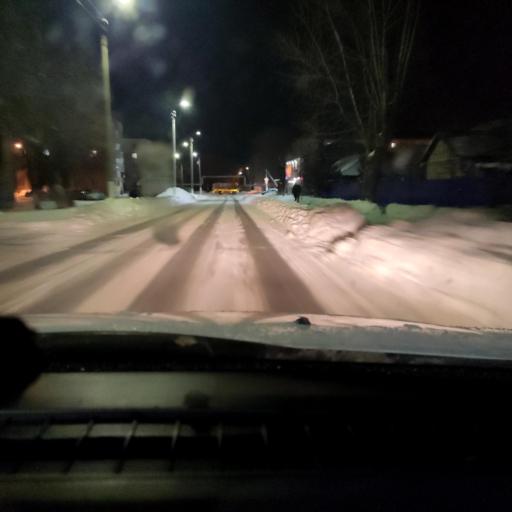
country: RU
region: Samara
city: Chapayevsk
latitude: 52.9601
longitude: 49.6880
